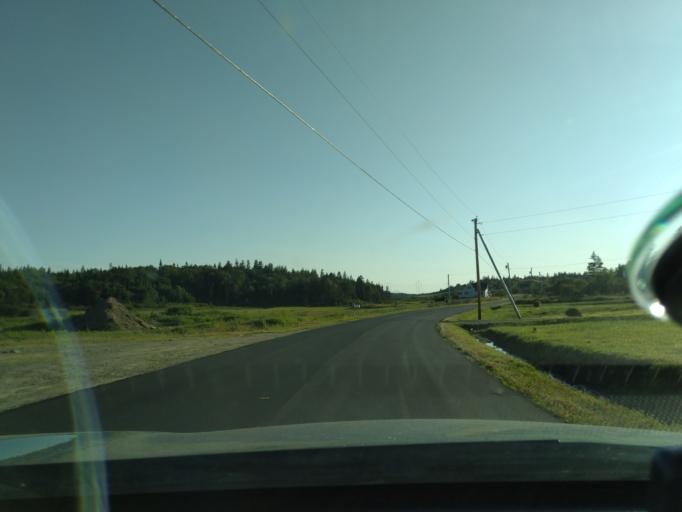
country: US
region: Maine
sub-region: Washington County
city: Machiasport
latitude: 44.6831
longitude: -67.1809
